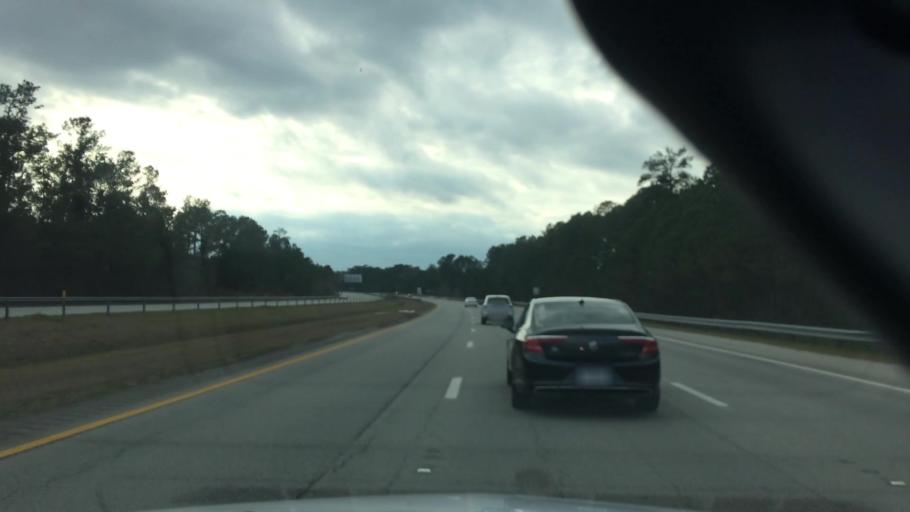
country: US
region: South Carolina
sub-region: Horry County
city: North Myrtle Beach
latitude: 33.8711
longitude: -78.6885
